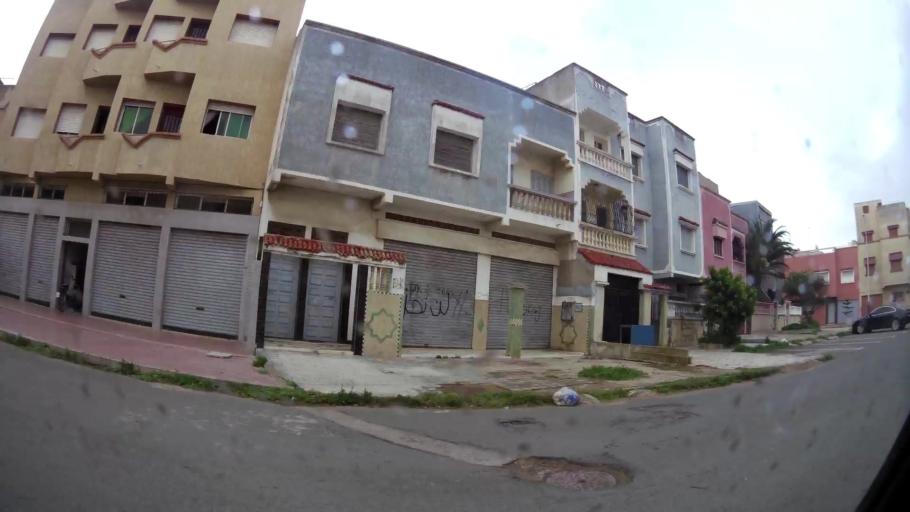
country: MA
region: Doukkala-Abda
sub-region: El-Jadida
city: El Jadida
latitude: 33.2502
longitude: -8.5251
